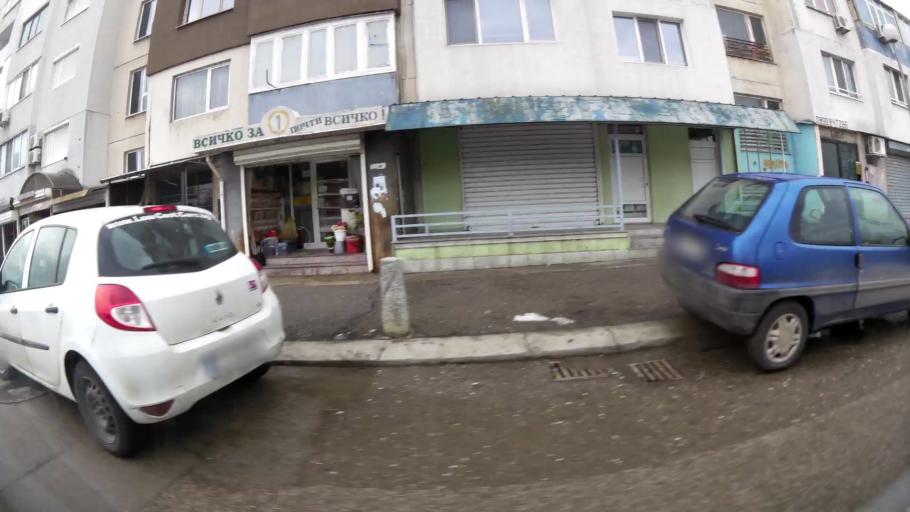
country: BG
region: Sofia-Capital
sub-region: Stolichna Obshtina
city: Sofia
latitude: 42.7376
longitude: 23.2705
